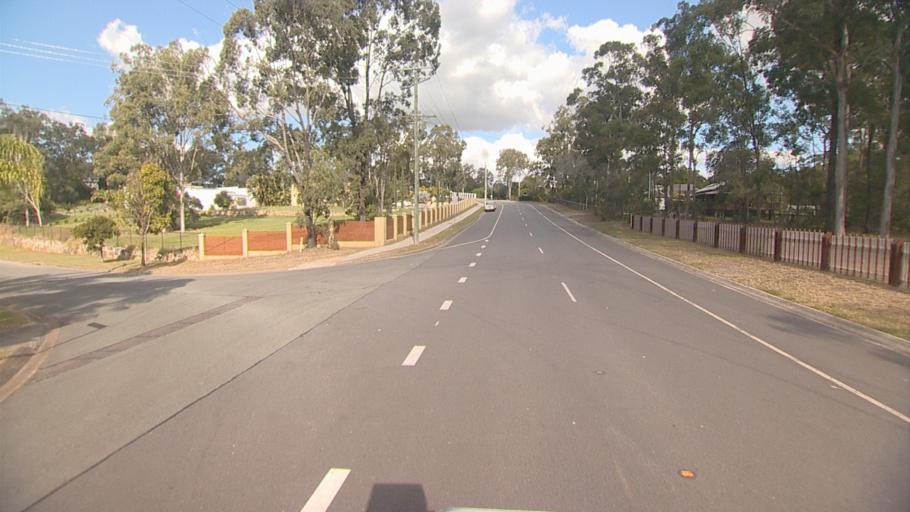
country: AU
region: Queensland
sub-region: Logan
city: Beenleigh
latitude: -27.6687
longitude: 153.2219
